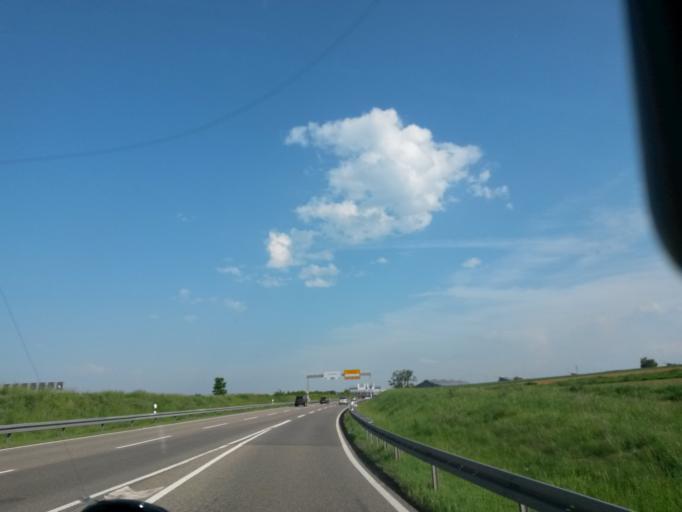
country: DE
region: Baden-Wuerttemberg
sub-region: Regierungsbezirk Stuttgart
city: Leinfelden-Echterdingen
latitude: 48.7016
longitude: 9.1783
